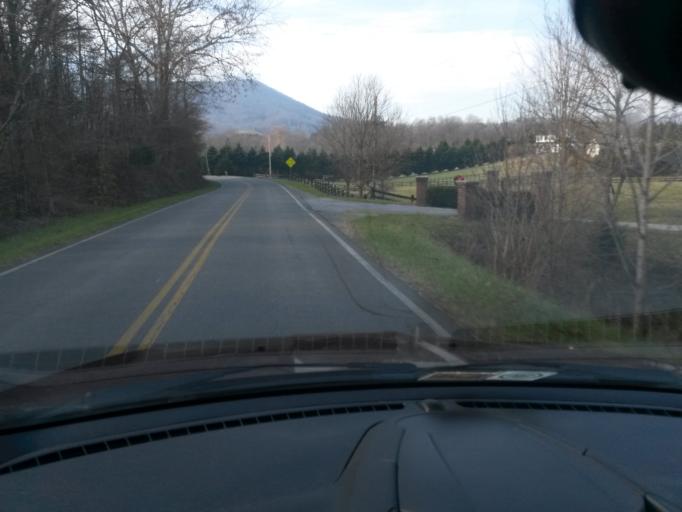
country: US
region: Virginia
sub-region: Botetourt County
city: Daleville
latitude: 37.4531
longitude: -79.9573
